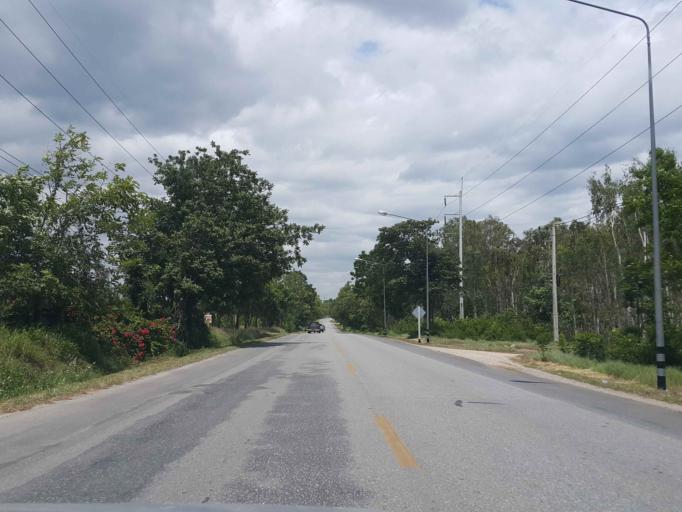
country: TH
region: Lamphun
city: Ban Hong
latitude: 18.3754
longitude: 98.8149
